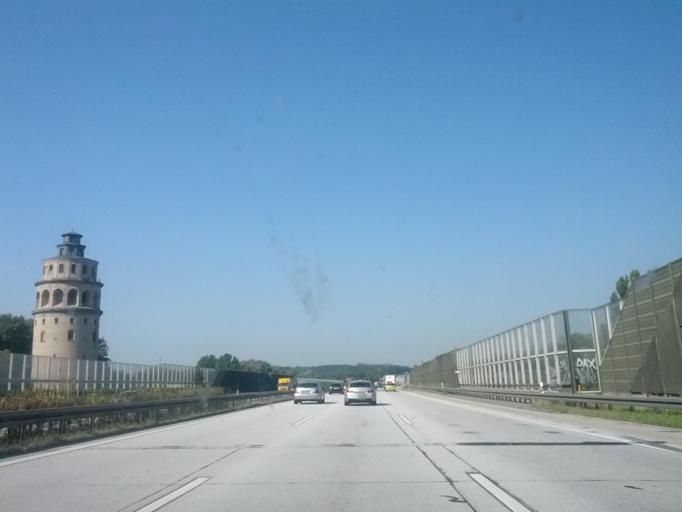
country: DE
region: Brandenburg
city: Wildau
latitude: 52.3111
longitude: 13.6495
